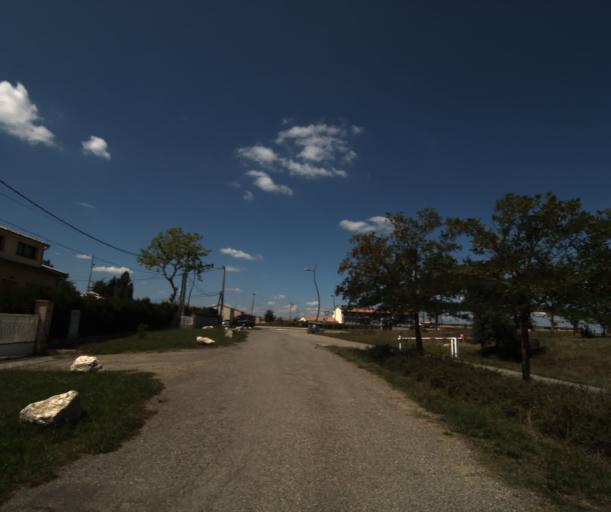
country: FR
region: Midi-Pyrenees
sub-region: Departement de la Haute-Garonne
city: Saint-Lys
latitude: 43.5196
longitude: 1.1896
